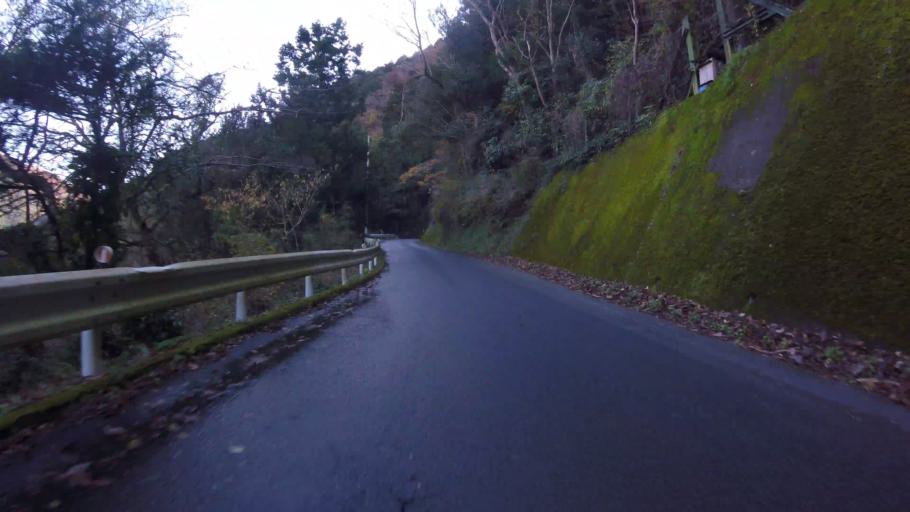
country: JP
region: Shizuoka
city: Shimoda
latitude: 34.7666
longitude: 138.9639
